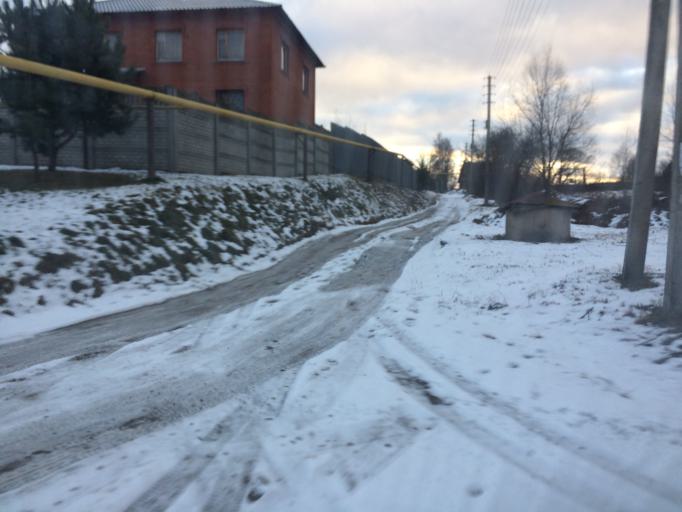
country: RU
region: Tula
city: Cherepet'
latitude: 54.1161
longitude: 36.3490
